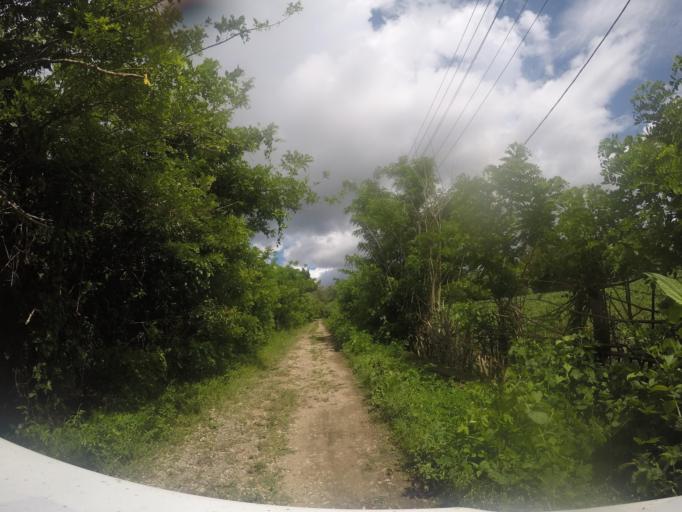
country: TL
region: Lautem
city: Lospalos
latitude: -8.4943
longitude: 127.0085
